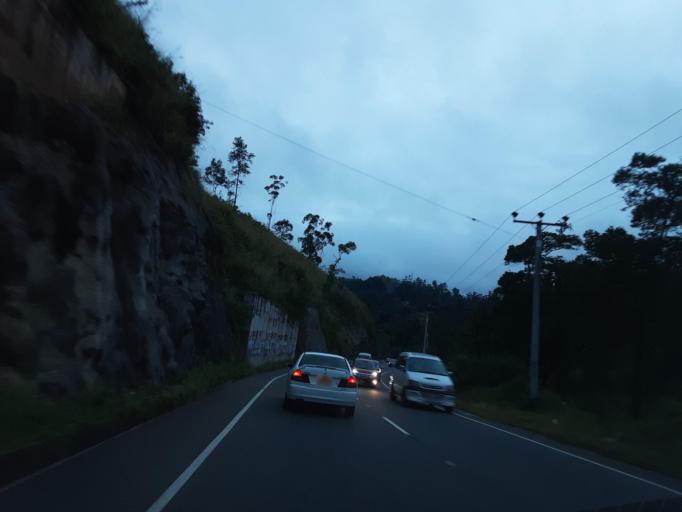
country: LK
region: Uva
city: Haputale
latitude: 6.9103
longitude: 80.9289
